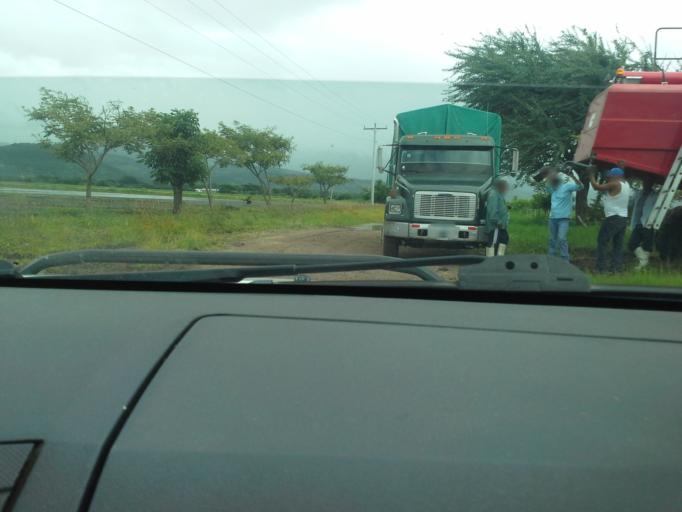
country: NI
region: Matagalpa
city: Ciudad Dario
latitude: 12.8576
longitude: -86.1830
